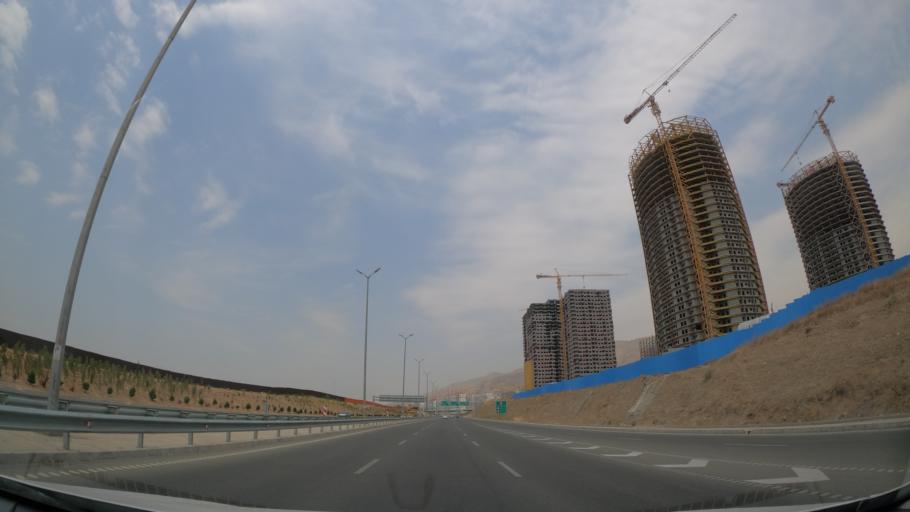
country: IR
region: Tehran
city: Shahr-e Qods
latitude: 35.7473
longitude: 51.1805
